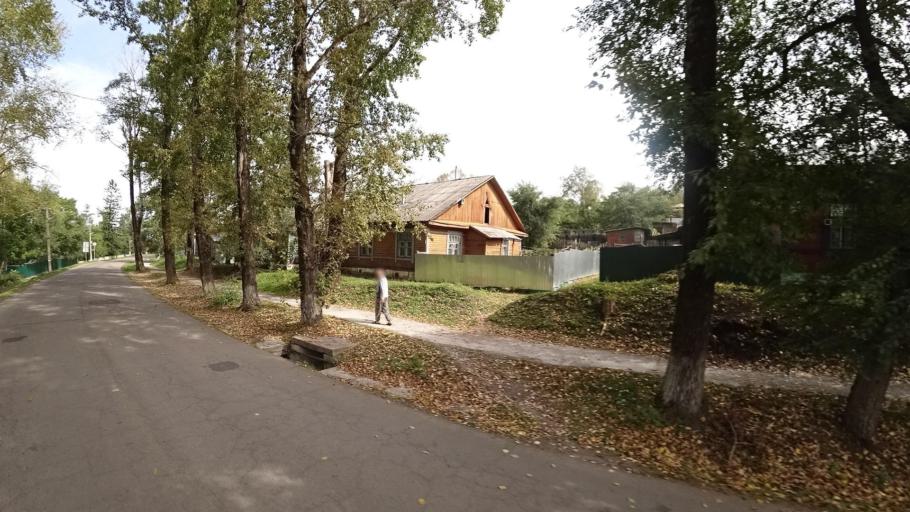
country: RU
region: Jewish Autonomous Oblast
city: Khingansk
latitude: 49.0141
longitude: 131.0596
